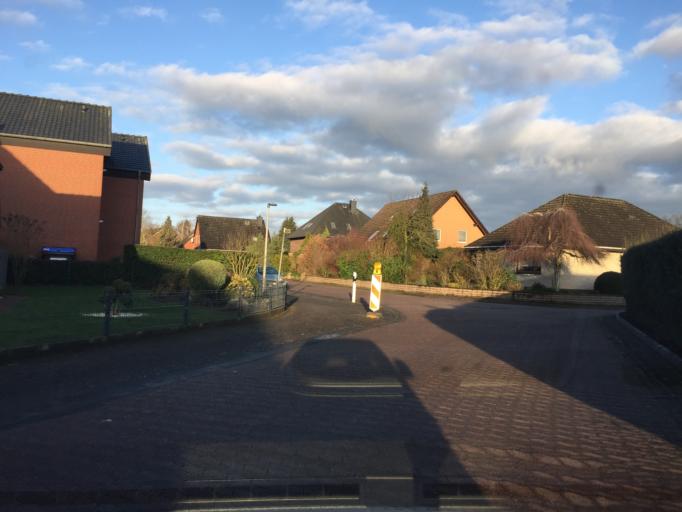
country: DE
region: Lower Saxony
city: Hassel
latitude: 52.6864
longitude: 8.8254
